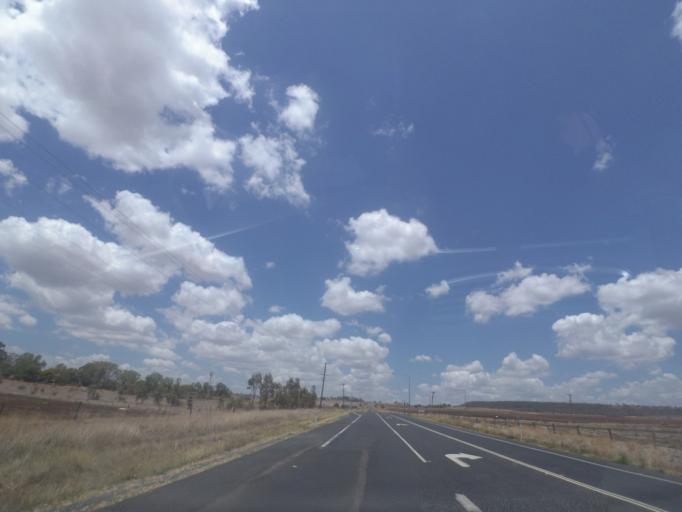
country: AU
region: Queensland
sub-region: Toowoomba
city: Top Camp
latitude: -27.7162
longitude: 151.9114
